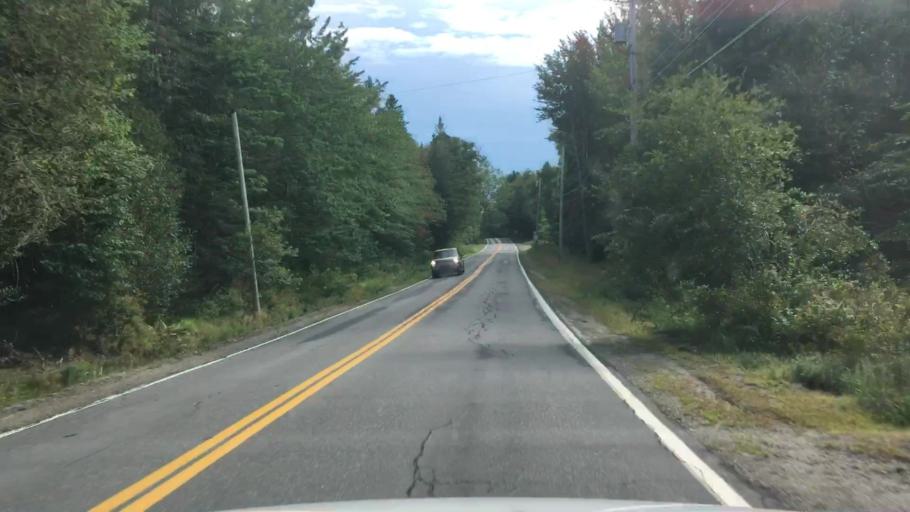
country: US
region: Maine
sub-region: Hancock County
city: Ellsworth
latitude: 44.4827
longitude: -68.4203
